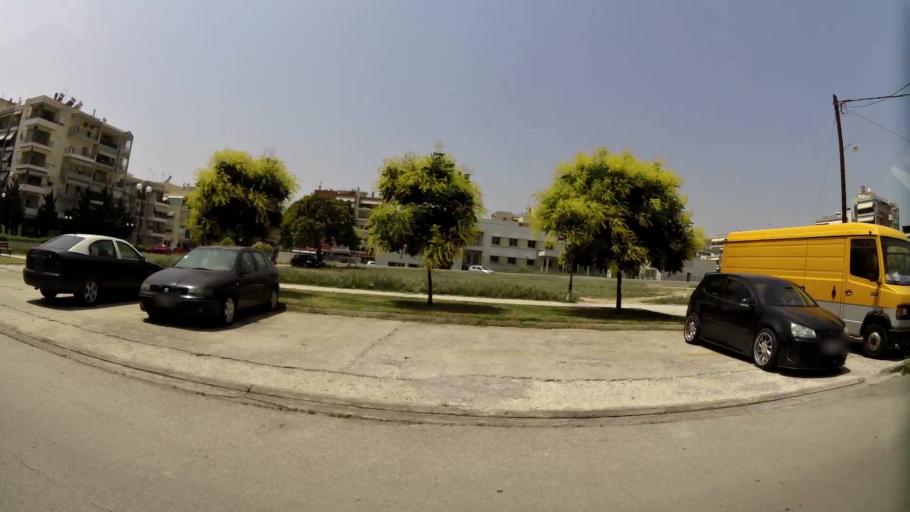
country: GR
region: Central Macedonia
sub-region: Nomos Thessalonikis
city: Evosmos
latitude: 40.6670
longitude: 22.9062
